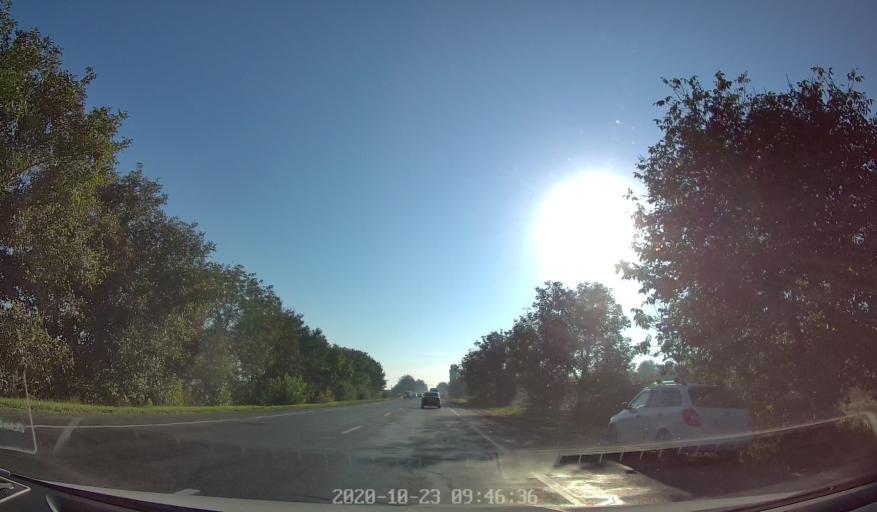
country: MD
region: Chisinau
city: Singera
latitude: 46.9116
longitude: 29.0909
